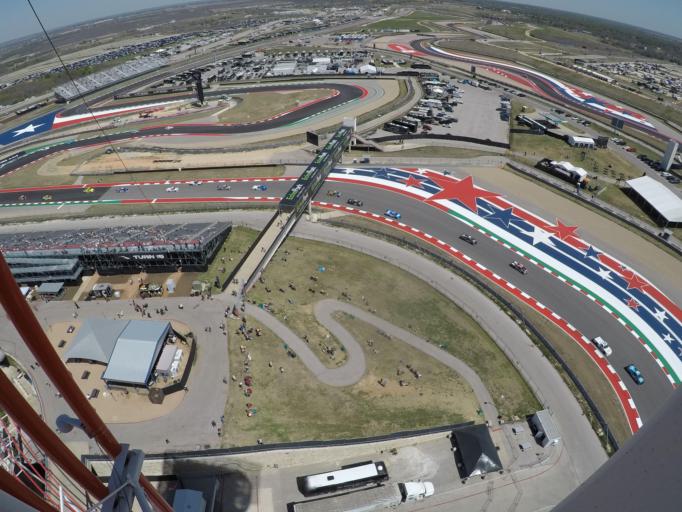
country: US
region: Texas
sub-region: Travis County
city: Garfield
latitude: 30.1349
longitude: -97.6381
